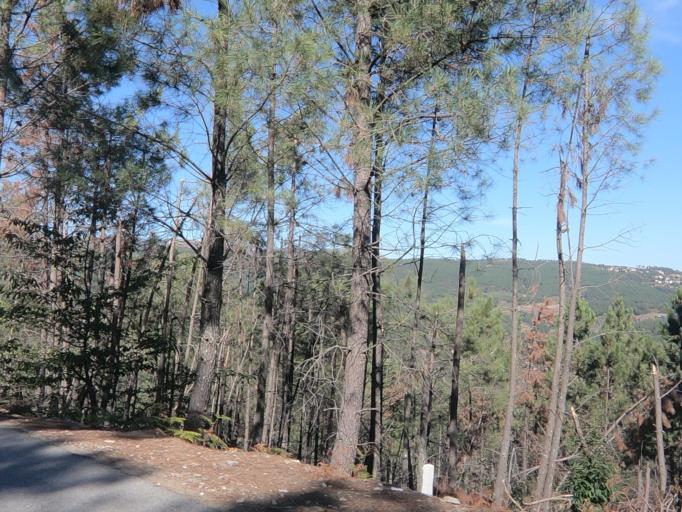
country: PT
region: Vila Real
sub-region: Santa Marta de Penaguiao
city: Santa Marta de Penaguiao
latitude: 41.2517
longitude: -7.8459
